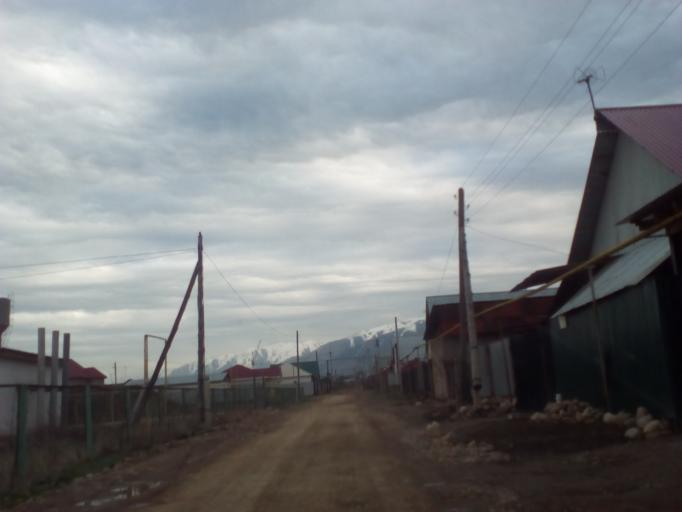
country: KZ
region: Almaty Oblysy
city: Burunday
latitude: 43.1809
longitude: 76.3982
